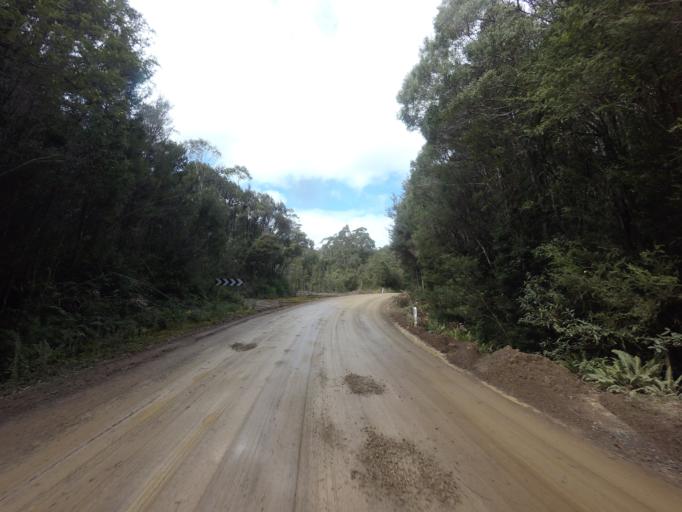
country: AU
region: Tasmania
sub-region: Huon Valley
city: Geeveston
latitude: -43.4059
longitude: 146.8683
